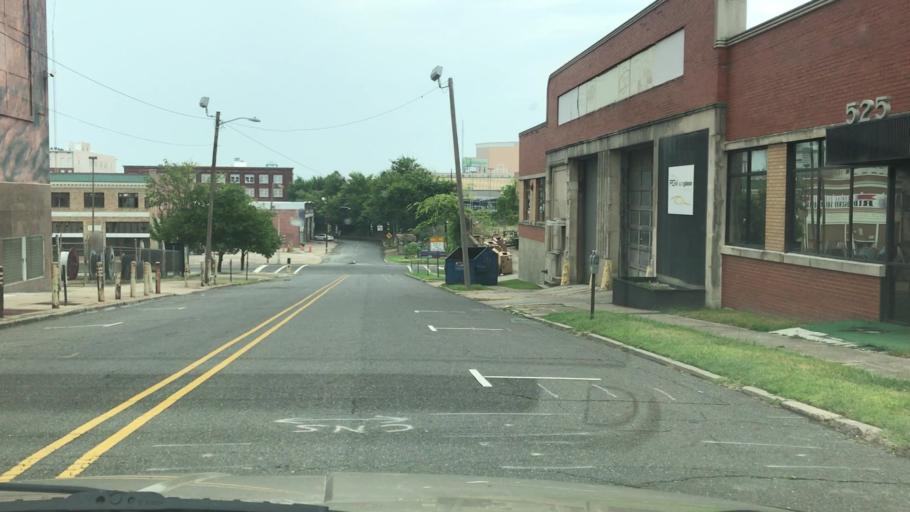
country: US
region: Louisiana
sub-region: Caddo Parish
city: Shreveport
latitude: 32.5098
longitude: -93.7481
